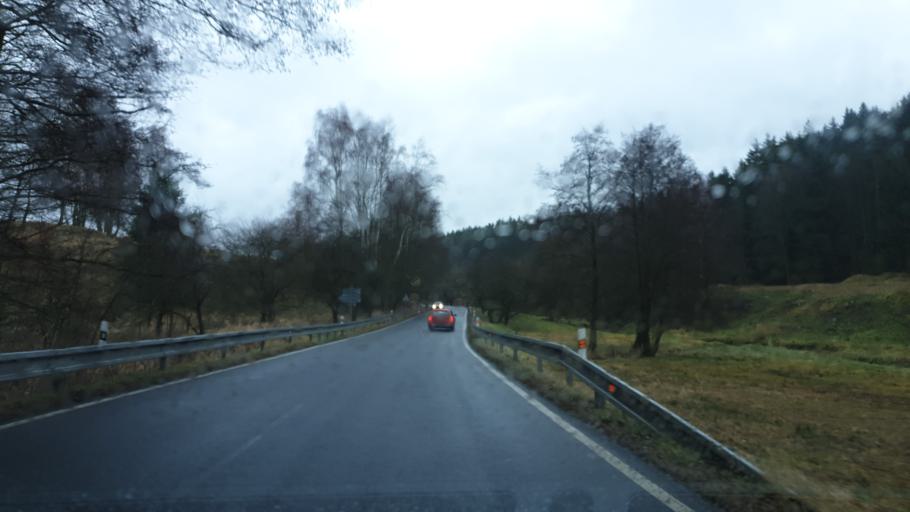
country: CZ
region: Karlovarsky
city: As
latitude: 50.2400
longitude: 12.1872
